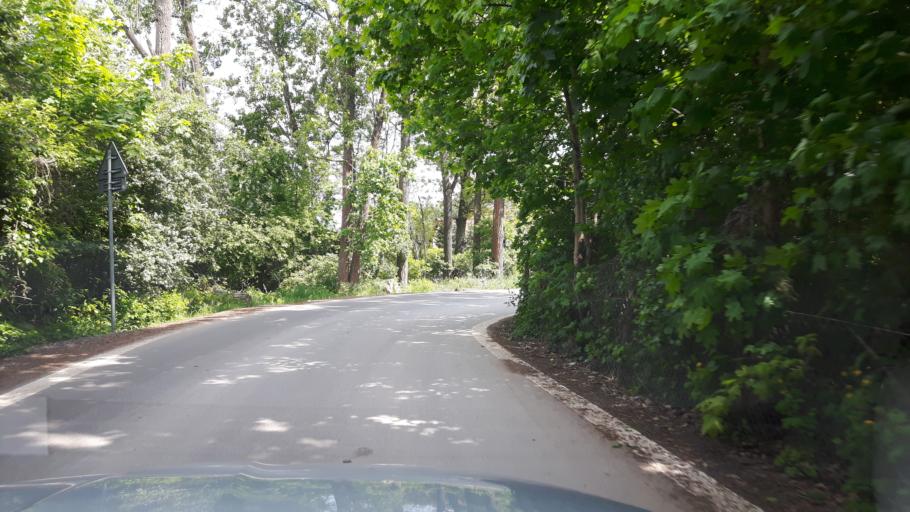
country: PL
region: Masovian Voivodeship
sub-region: Powiat legionowski
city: Stanislawow Pierwszy
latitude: 52.3385
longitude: 21.0340
